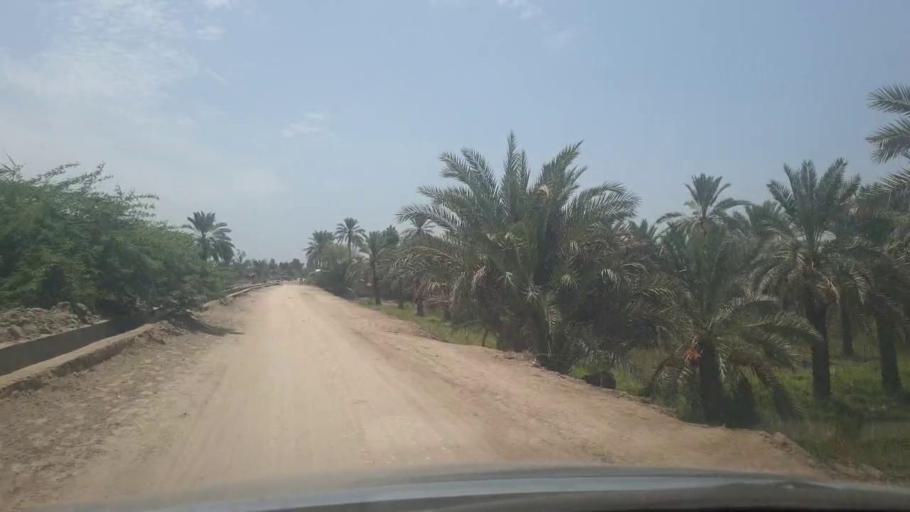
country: PK
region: Sindh
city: Kot Diji
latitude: 27.4146
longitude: 68.7404
